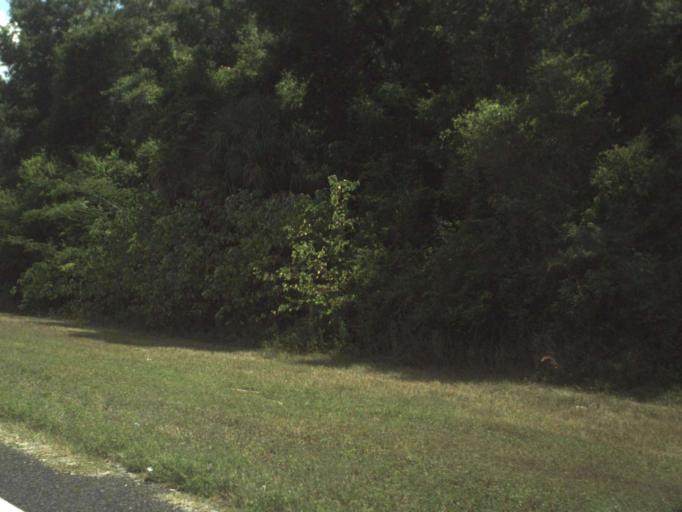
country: US
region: Florida
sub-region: Marion County
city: Ocala
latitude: 29.2212
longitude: -82.1469
